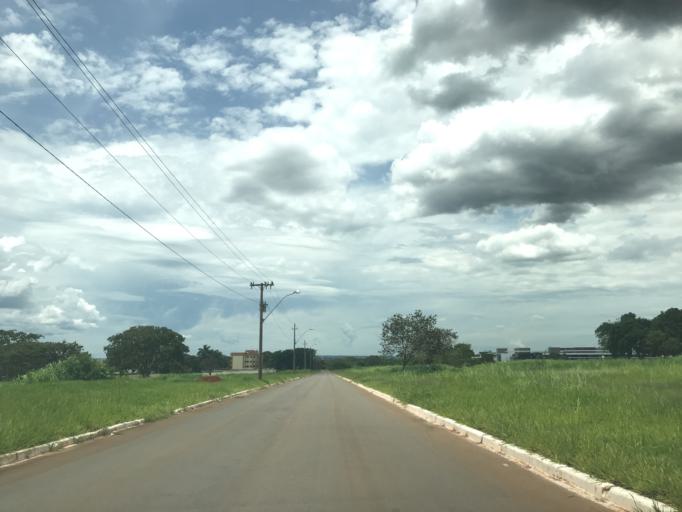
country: BR
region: Federal District
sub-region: Brasilia
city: Brasilia
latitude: -15.8329
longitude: -47.9049
